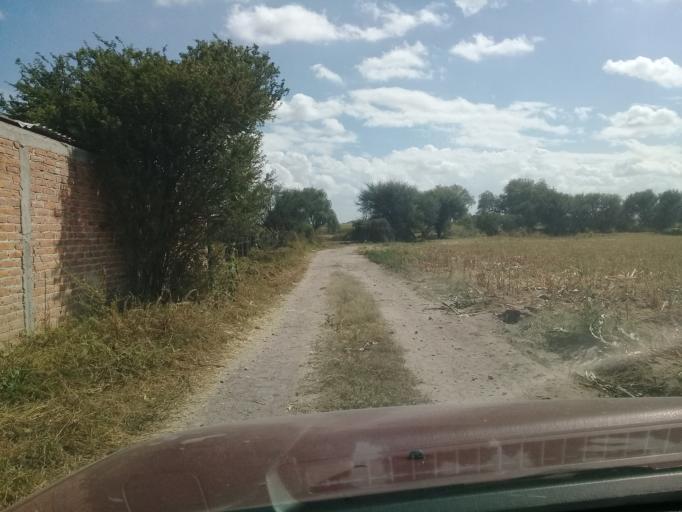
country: MX
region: Aguascalientes
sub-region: Aguascalientes
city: Penuelas (El Cienegal)
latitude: 21.7699
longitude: -102.3101
